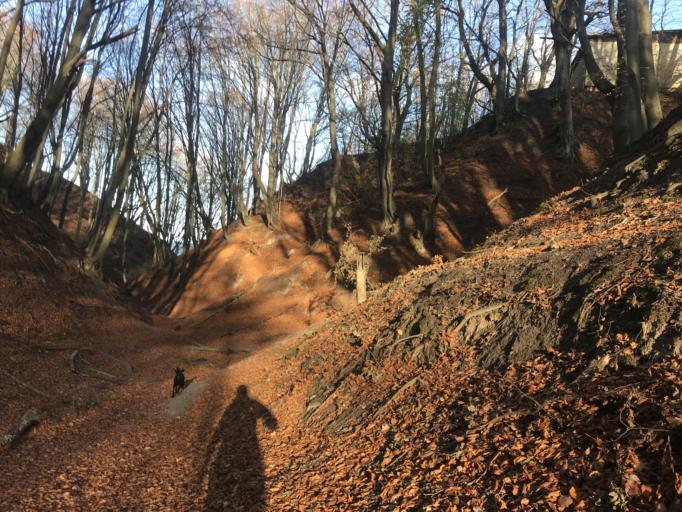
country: PL
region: Pomeranian Voivodeship
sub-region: Powiat pucki
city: Jastrzebia Gora
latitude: 54.8331
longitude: 18.3270
